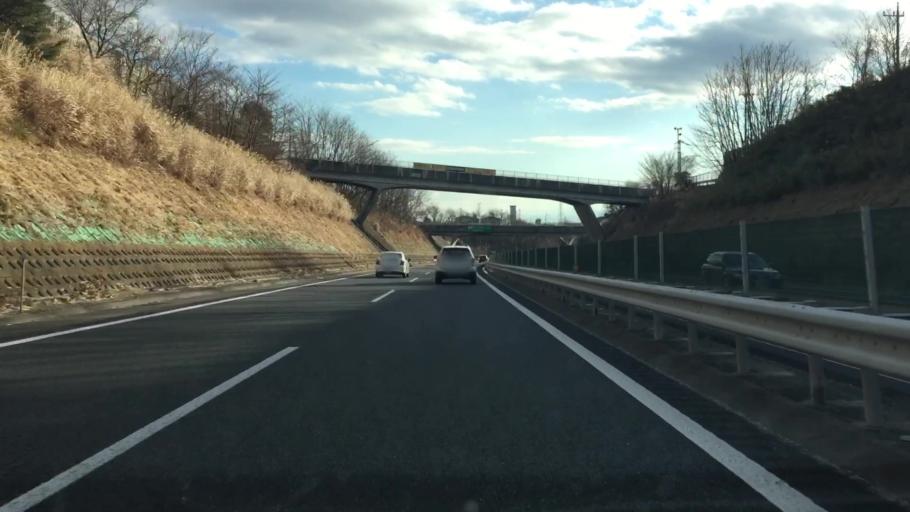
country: JP
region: Gunma
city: Shibukawa
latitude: 36.4946
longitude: 139.0311
